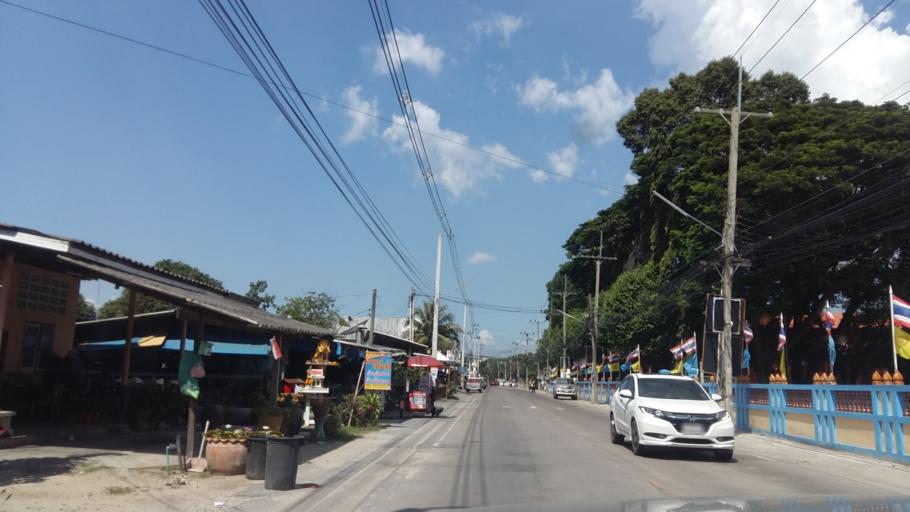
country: TH
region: Chon Buri
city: Chon Buri
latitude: 13.3151
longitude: 100.9307
